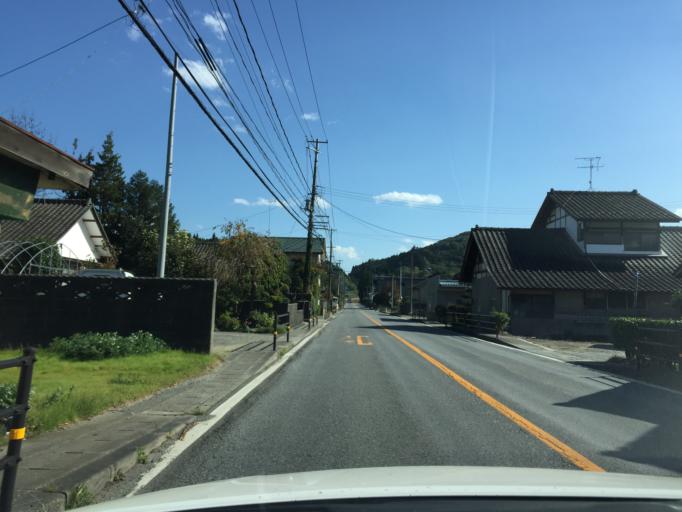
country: JP
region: Fukushima
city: Iwaki
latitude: 37.1005
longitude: 140.7747
